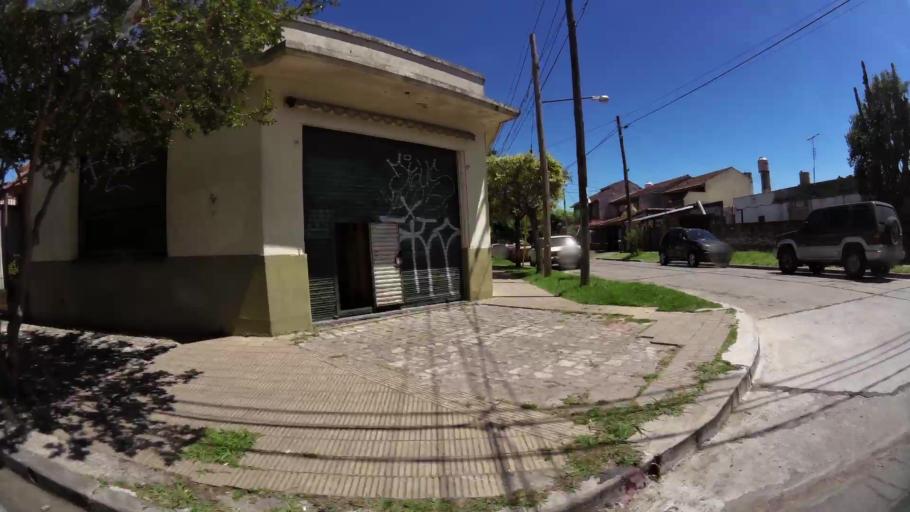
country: AR
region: Buenos Aires
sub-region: Partido de San Isidro
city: San Isidro
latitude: -34.5060
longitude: -58.5515
